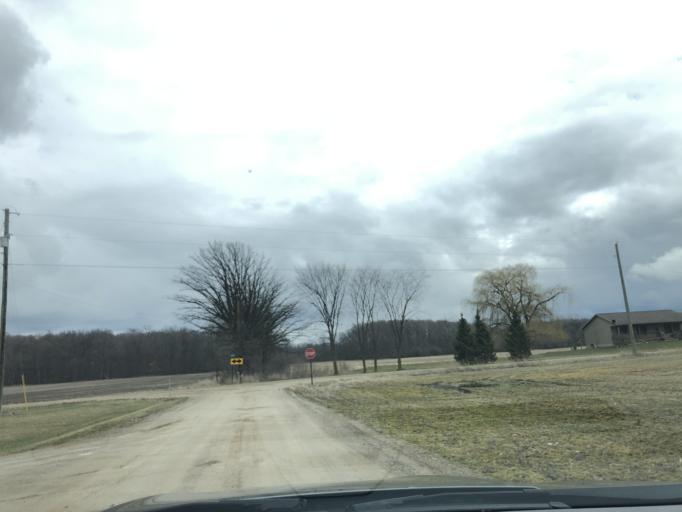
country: US
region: Michigan
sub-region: Clinton County
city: Saint Johns
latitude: 43.0897
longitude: -84.6114
